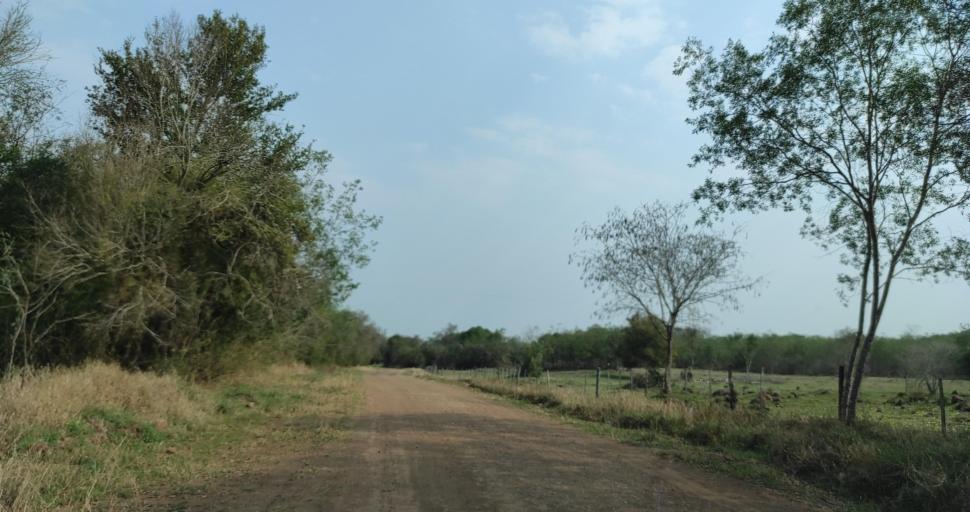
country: AR
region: Misiones
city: Cerro Cora
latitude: -27.5597
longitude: -55.5813
